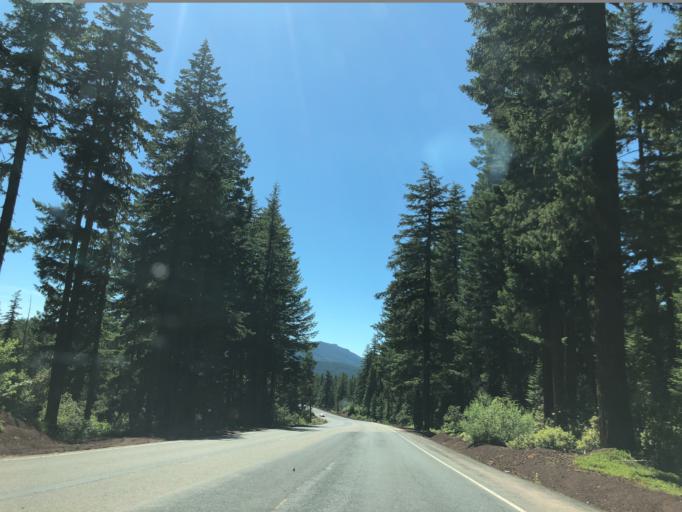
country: US
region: Oregon
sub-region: Deschutes County
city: Sisters
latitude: 44.4327
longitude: -121.9654
